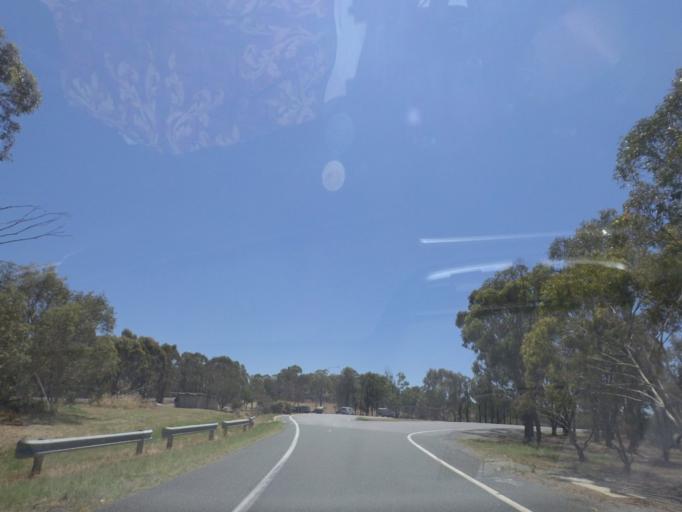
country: AU
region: Victoria
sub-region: Benalla
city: Benalla
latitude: -36.7147
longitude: 145.6343
